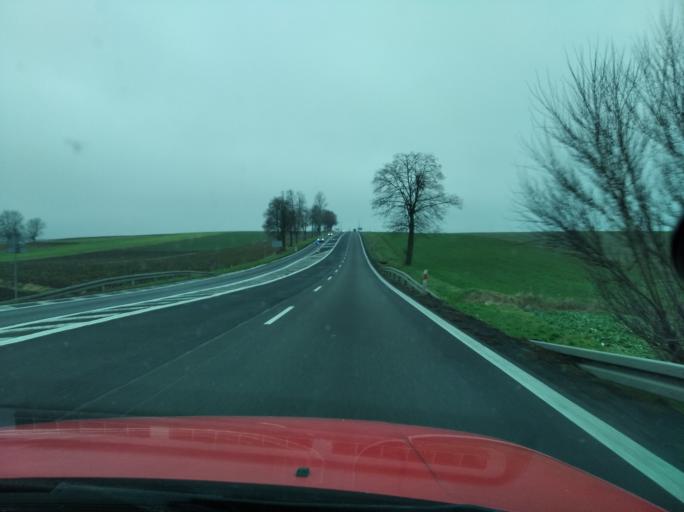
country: PL
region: Subcarpathian Voivodeship
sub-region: Powiat jaroslawski
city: Wierzbna
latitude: 50.0339
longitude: 22.5961
